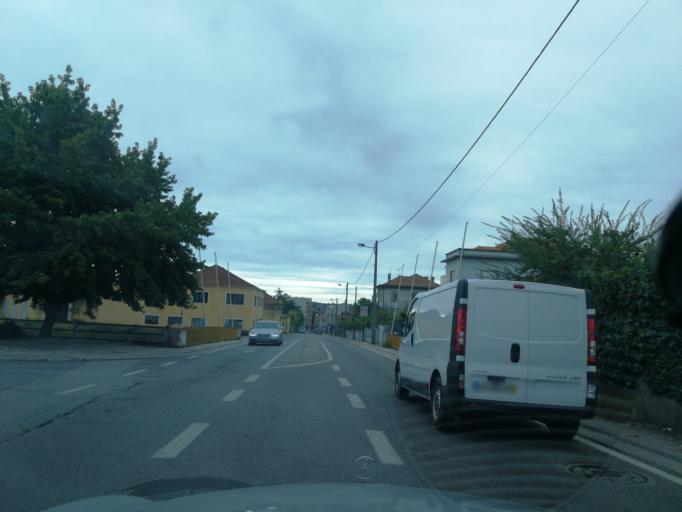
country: PT
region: Aveiro
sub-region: Agueda
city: Agueda
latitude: 40.5776
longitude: -8.4500
